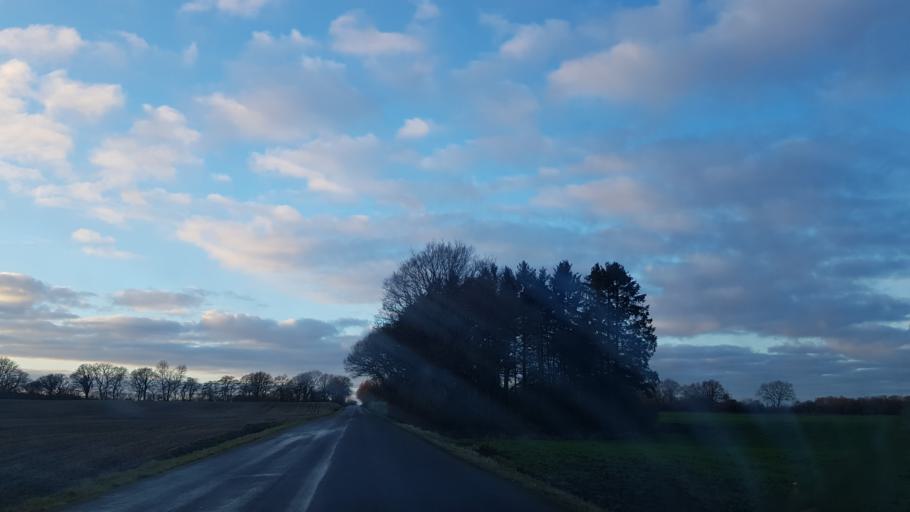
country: DK
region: South Denmark
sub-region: Kolding Kommune
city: Vamdrup
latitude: 55.3656
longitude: 9.3215
